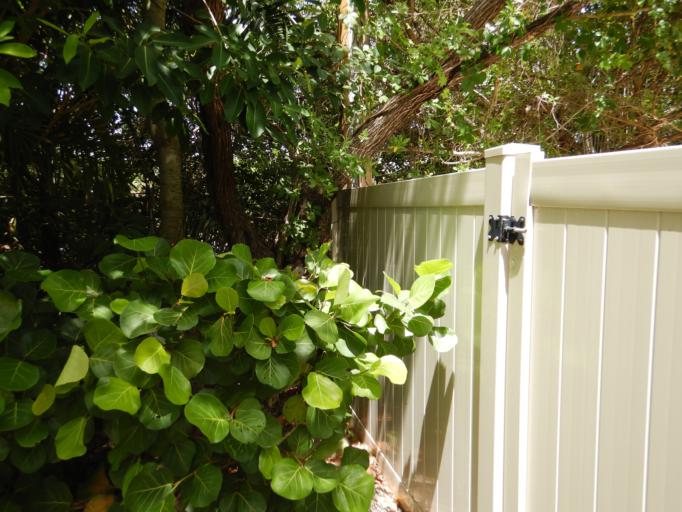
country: US
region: Florida
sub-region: Sarasota County
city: Vamo
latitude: 27.2273
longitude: -82.5208
